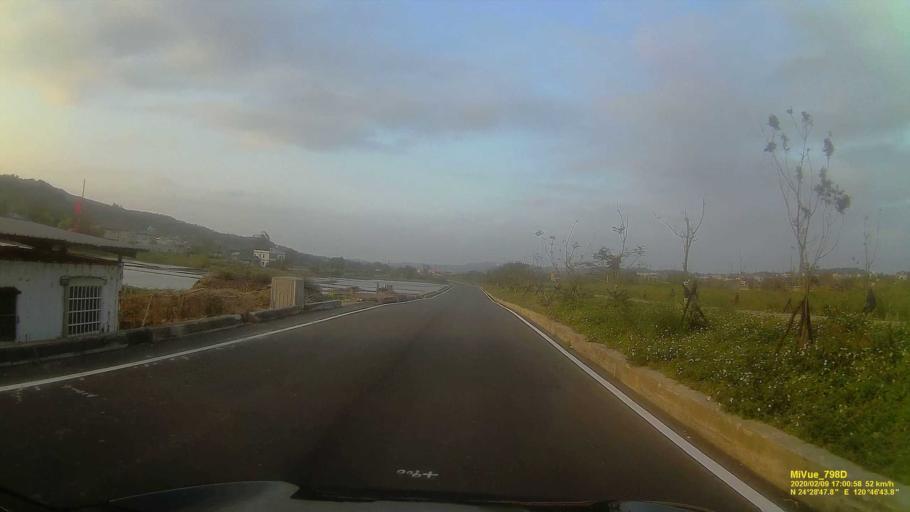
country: TW
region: Taiwan
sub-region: Miaoli
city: Miaoli
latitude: 24.4802
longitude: 120.7789
